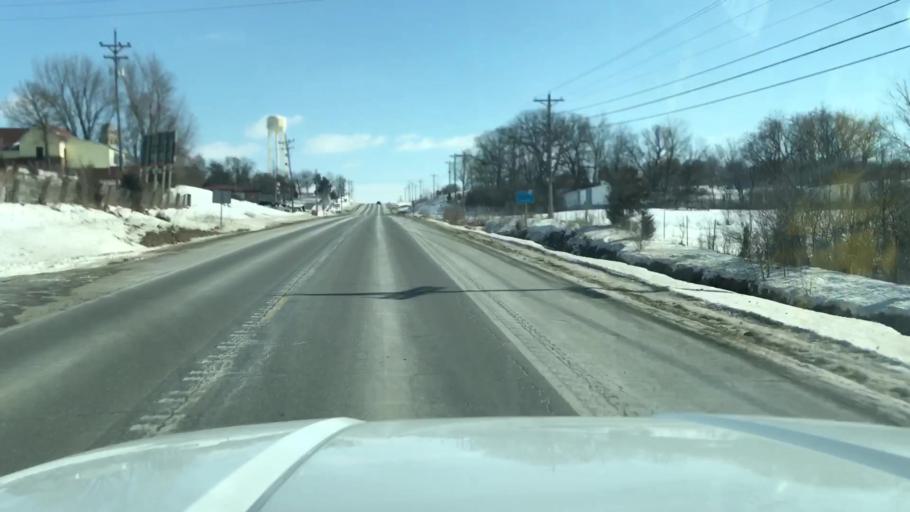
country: US
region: Missouri
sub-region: Nodaway County
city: Maryville
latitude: 40.3448
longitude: -94.8184
